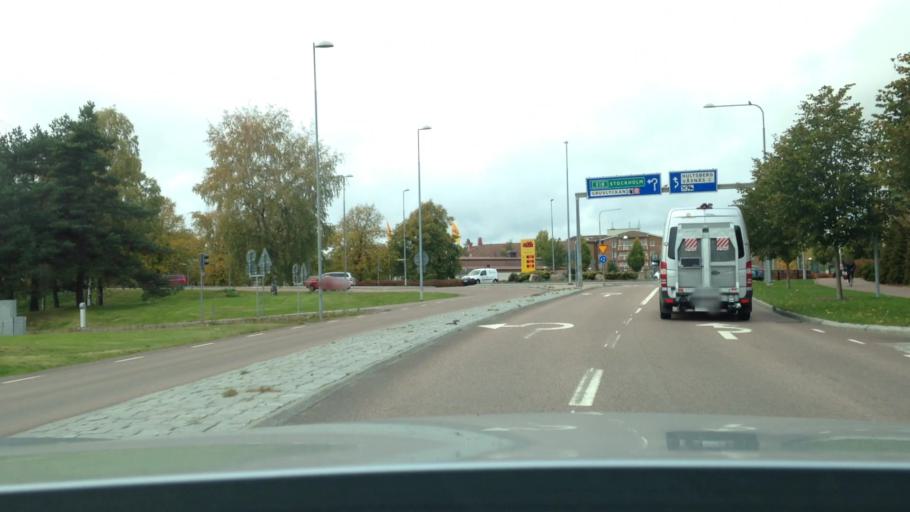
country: SE
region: Vaermland
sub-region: Karlstads Kommun
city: Karlstad
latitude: 59.3823
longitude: 13.4661
